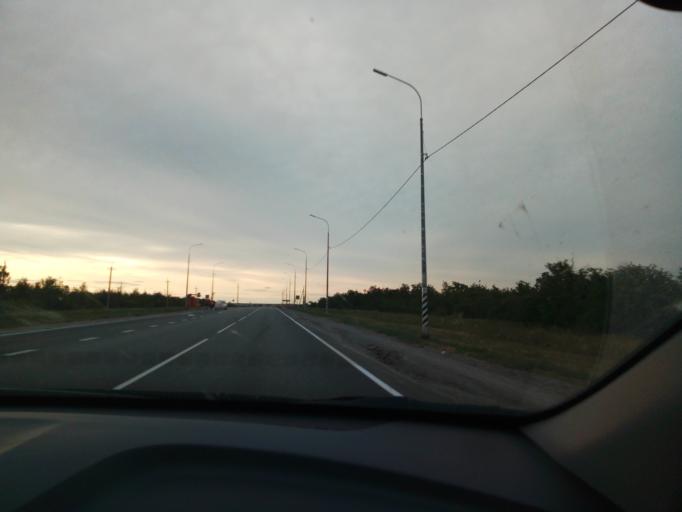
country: RU
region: Volgograd
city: Primorsk
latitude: 49.2340
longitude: 44.8989
